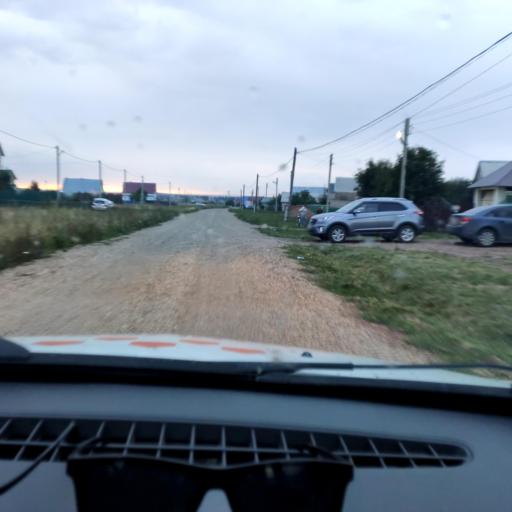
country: RU
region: Bashkortostan
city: Kabakovo
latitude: 54.5298
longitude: 56.1488
